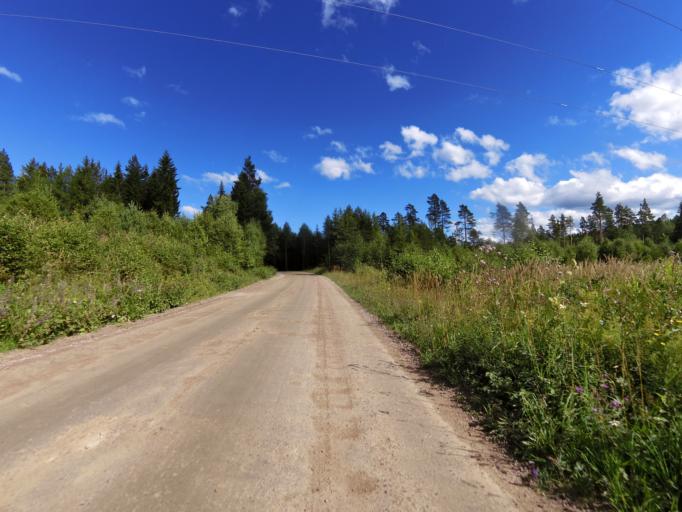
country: SE
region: Gaevleborg
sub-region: Hofors Kommun
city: Hofors
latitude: 60.5025
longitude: 16.3113
